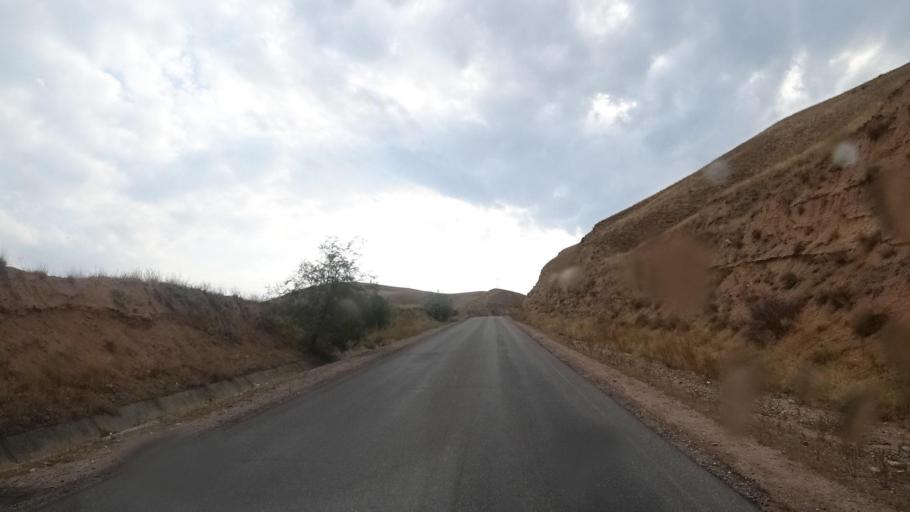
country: KG
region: Jalal-Abad
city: Toktogul
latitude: 41.8585
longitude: 73.0325
